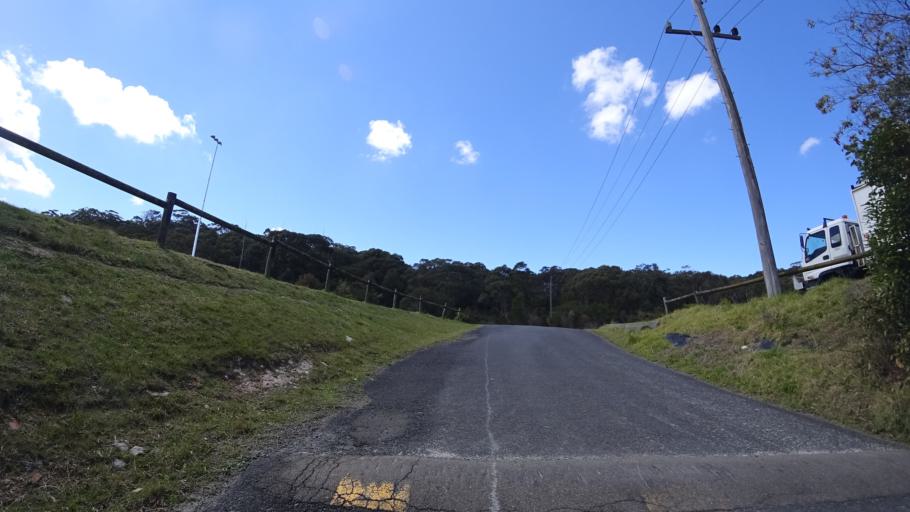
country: AU
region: New South Wales
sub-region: Warringah
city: Killarney Heights
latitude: -33.7601
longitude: 151.2266
